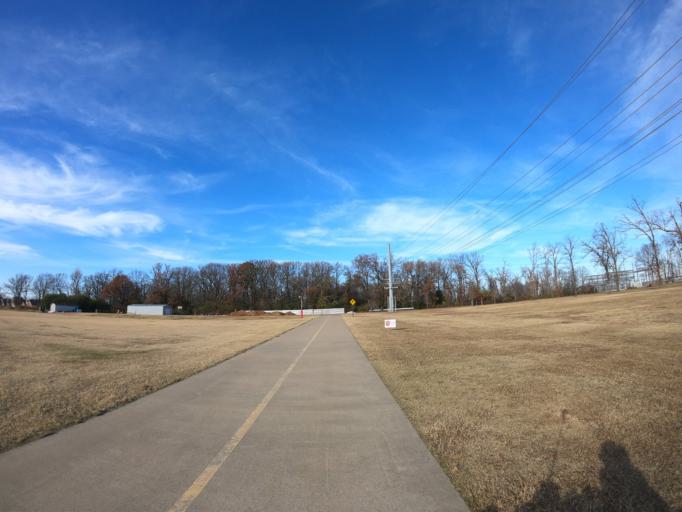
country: US
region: Arkansas
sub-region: Benton County
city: Lowell
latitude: 36.2807
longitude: -94.1696
